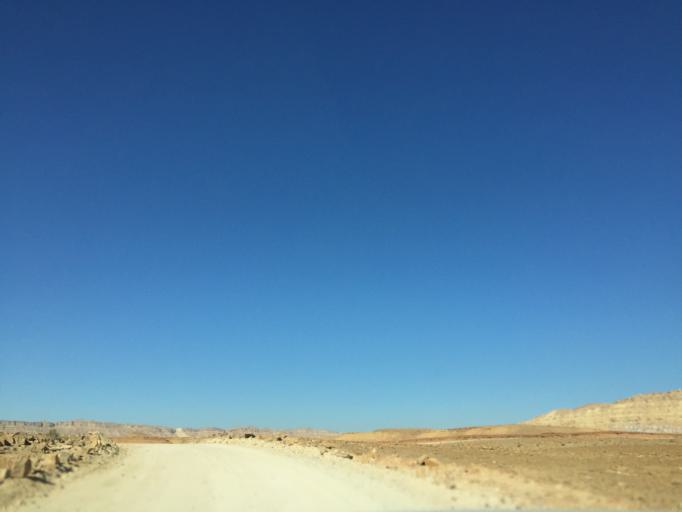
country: IL
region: Southern District
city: Mitzpe Ramon
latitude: 30.6187
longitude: 34.9306
